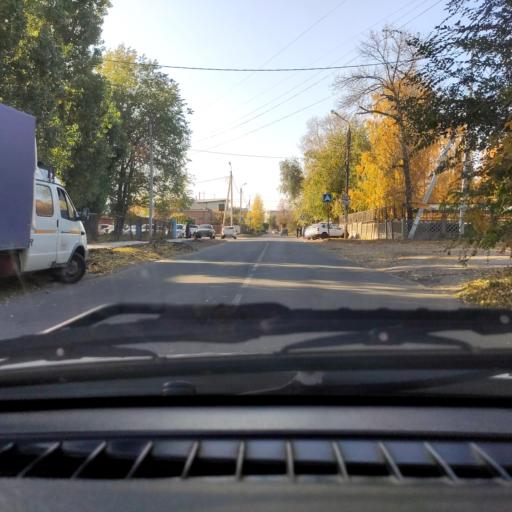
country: RU
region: Samara
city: Tol'yatti
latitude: 53.5246
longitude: 49.4198
